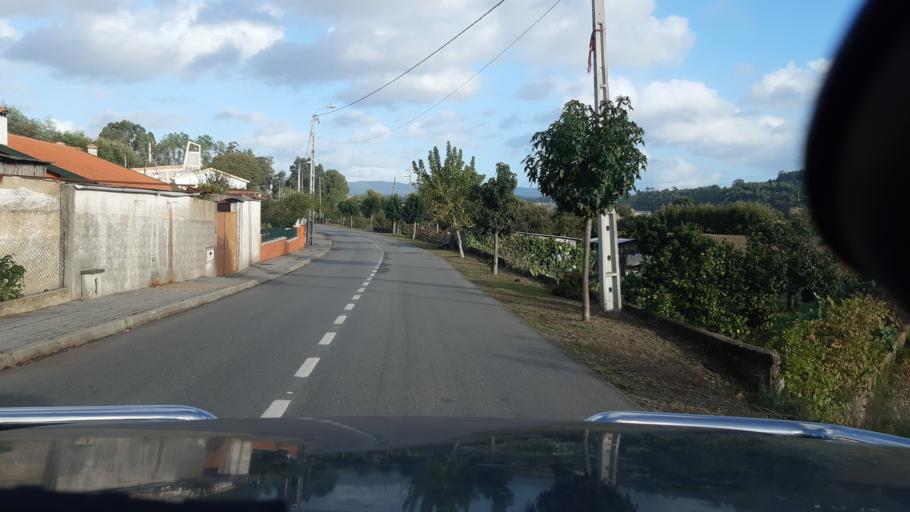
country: PT
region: Aveiro
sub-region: Agueda
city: Agueda
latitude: 40.5751
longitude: -8.4654
